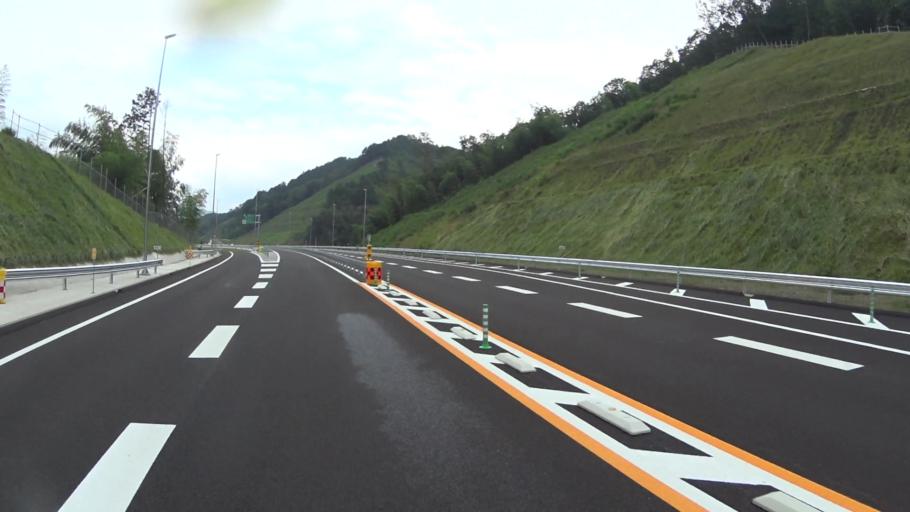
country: JP
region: Kyoto
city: Ayabe
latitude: 35.1887
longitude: 135.3598
